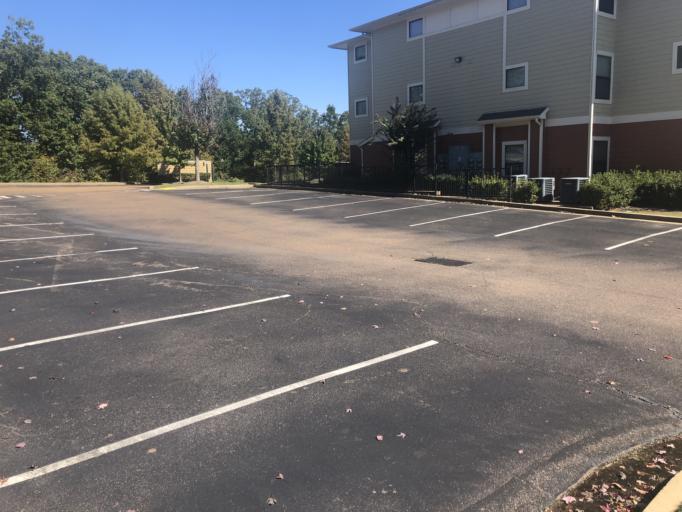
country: US
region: Mississippi
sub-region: Lafayette County
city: University
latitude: 34.3457
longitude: -89.5387
